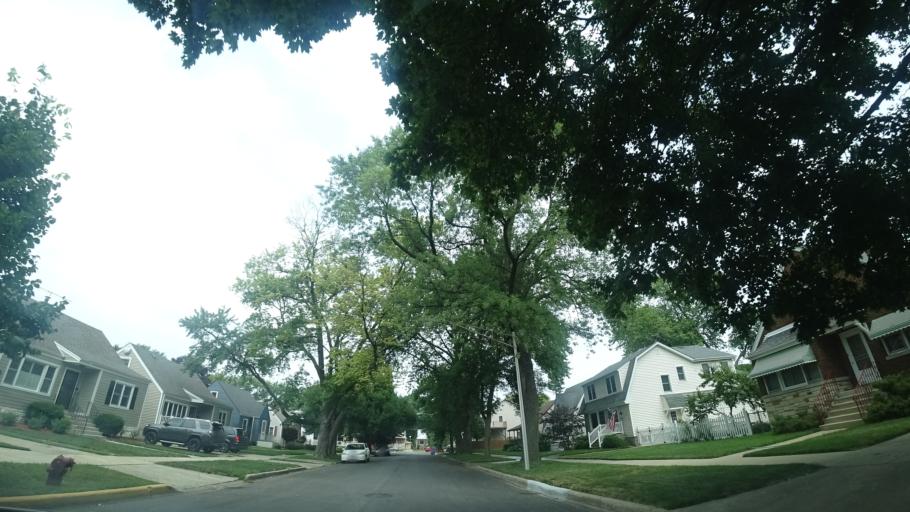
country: US
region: Illinois
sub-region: Cook County
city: Merrionette Park
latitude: 41.7013
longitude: -87.7146
